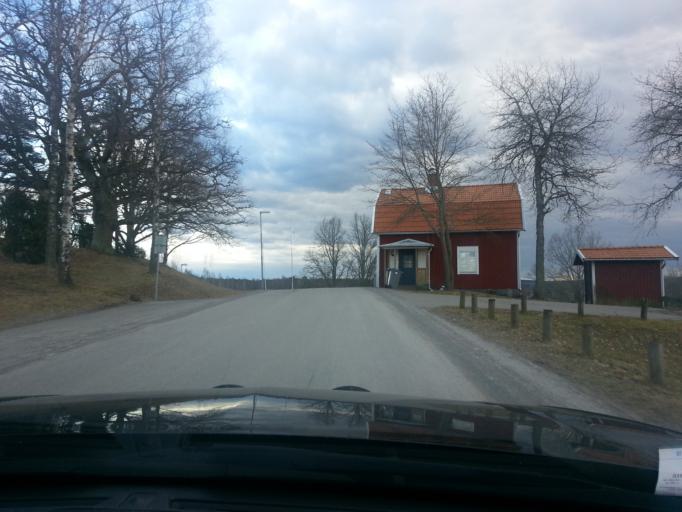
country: SE
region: Joenkoeping
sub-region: Vetlanda Kommun
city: Vetlanda
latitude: 57.4095
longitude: 15.0468
